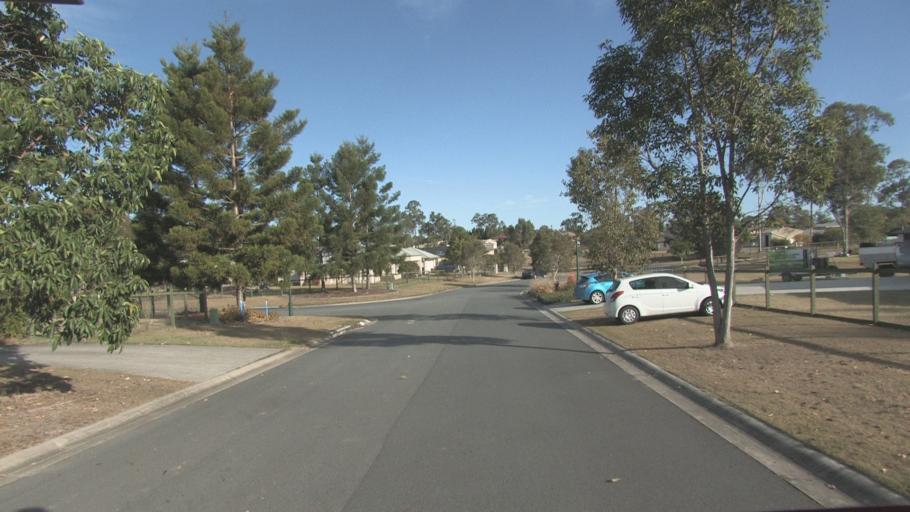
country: AU
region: Queensland
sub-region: Logan
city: North Maclean
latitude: -27.7973
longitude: 152.9644
